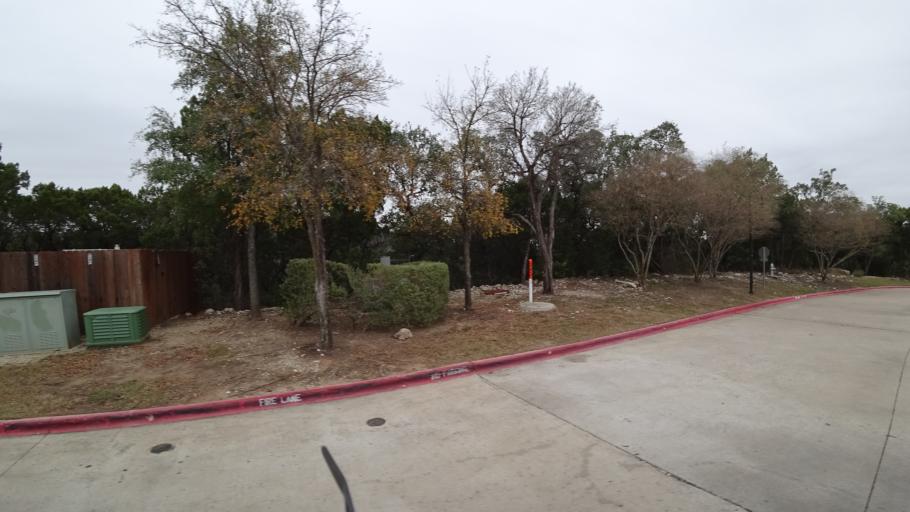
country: US
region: Texas
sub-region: Travis County
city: West Lake Hills
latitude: 30.3634
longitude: -97.7915
